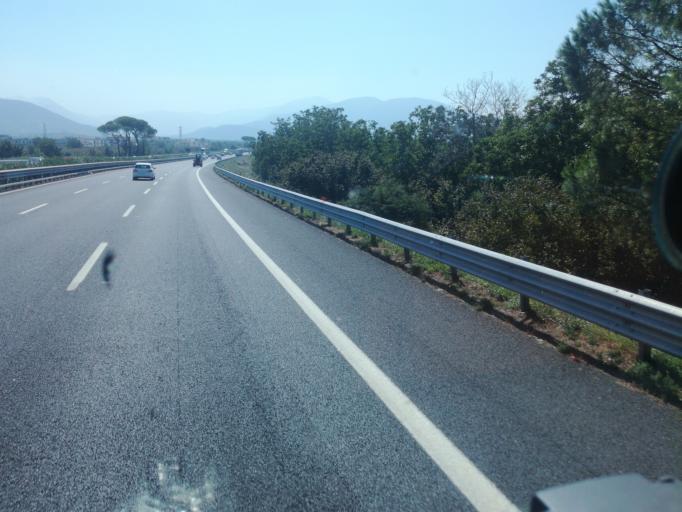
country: IT
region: Campania
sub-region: Provincia di Napoli
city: Nola
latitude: 40.9163
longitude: 14.5200
